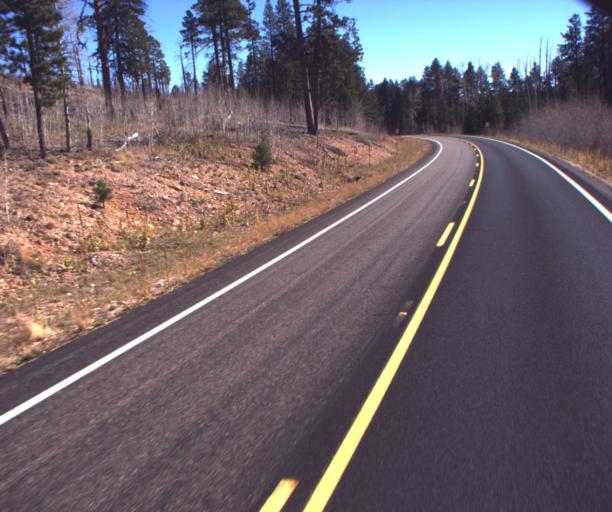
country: US
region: Arizona
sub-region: Coconino County
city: Grand Canyon
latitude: 36.5443
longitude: -112.1765
